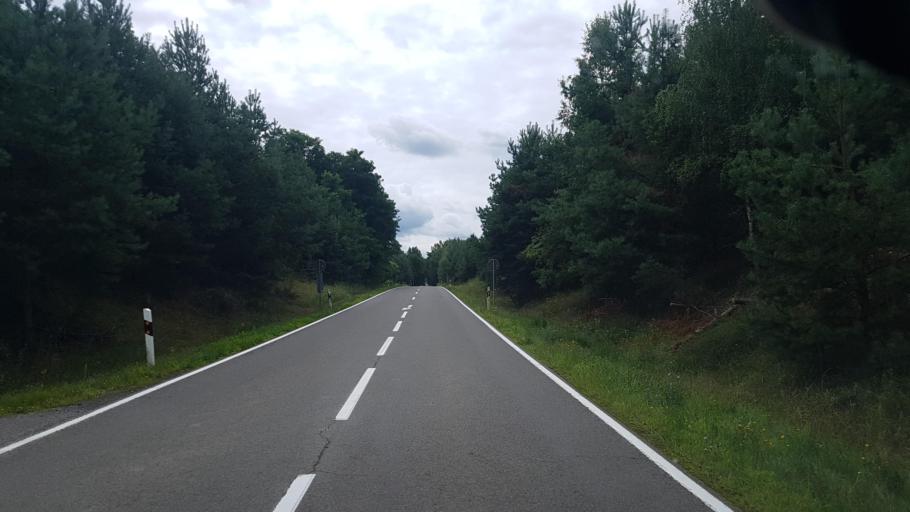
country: DE
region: Brandenburg
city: Spremberg
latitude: 51.6074
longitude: 14.3420
